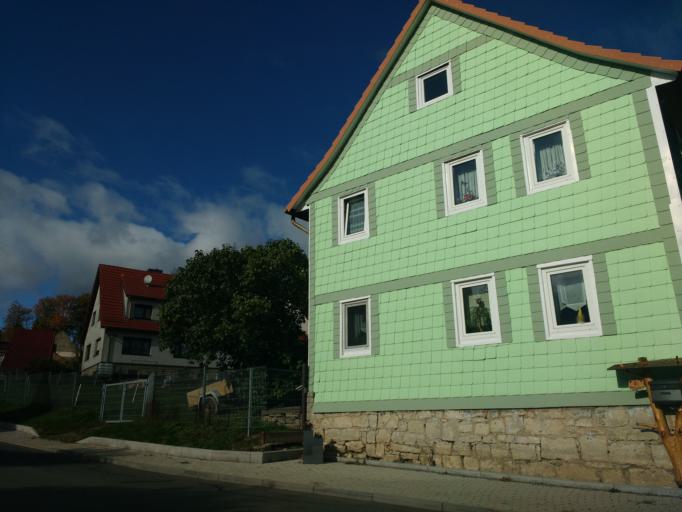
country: DE
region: Thuringia
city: Worbis
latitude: 51.4438
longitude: 10.3577
